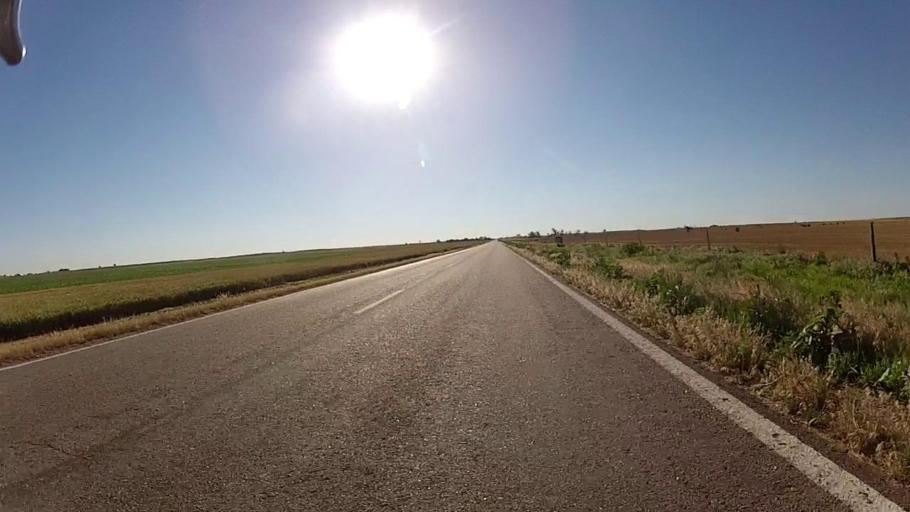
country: US
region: Kansas
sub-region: Ford County
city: Dodge City
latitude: 37.6459
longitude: -99.8119
